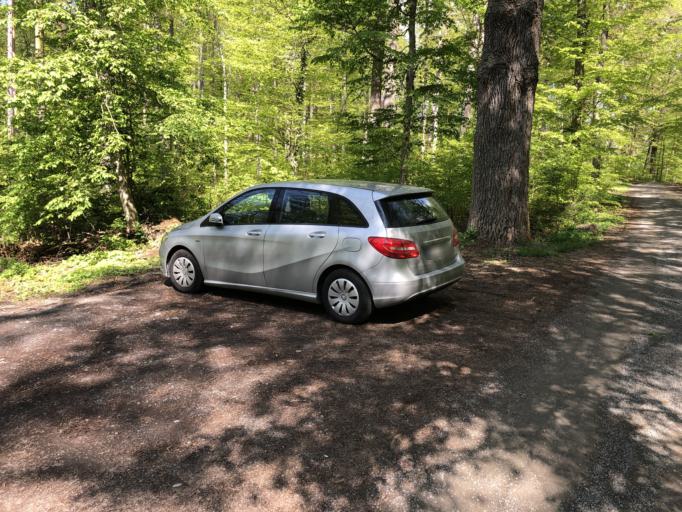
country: DE
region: Baden-Wuerttemberg
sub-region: Tuebingen Region
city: Tuebingen
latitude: 48.5502
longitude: 9.0076
